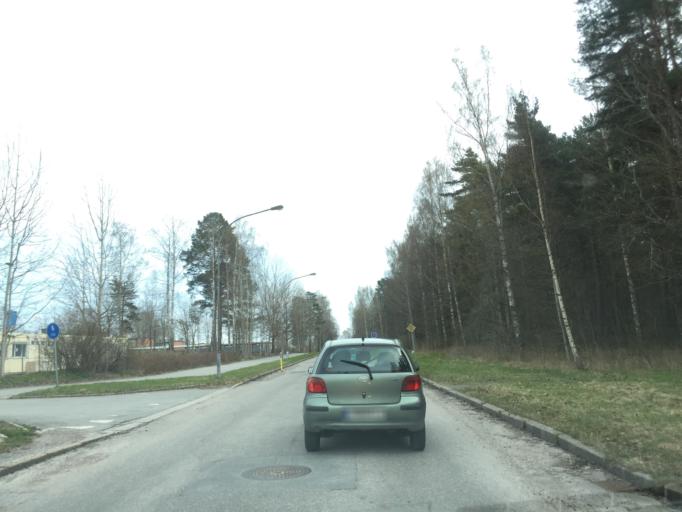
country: SE
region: OErebro
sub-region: Orebro Kommun
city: Orebro
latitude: 59.2949
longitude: 15.1880
